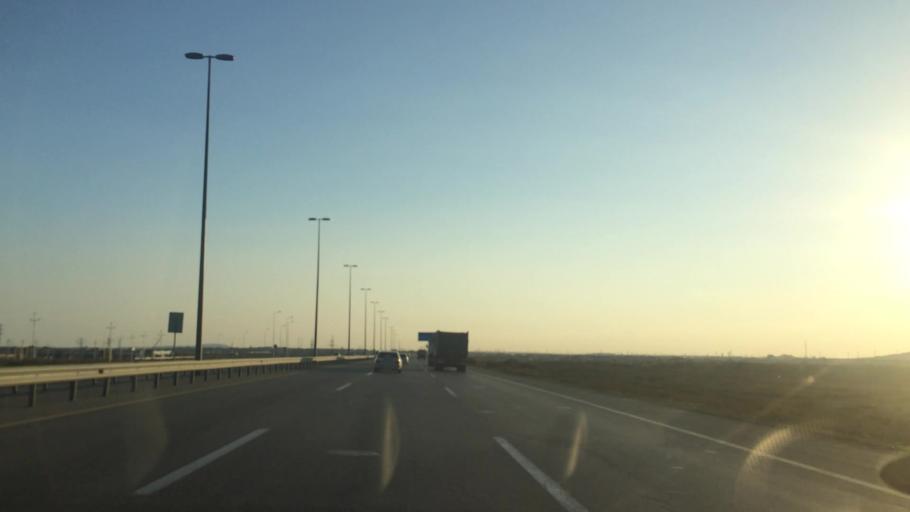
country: AZ
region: Baki
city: Qobustan
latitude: 39.9852
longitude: 49.4258
